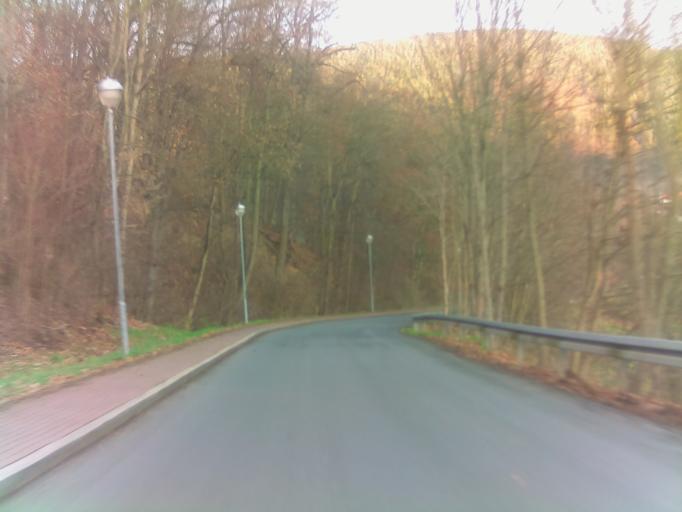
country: DE
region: Thuringia
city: Reinstadt
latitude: 50.7316
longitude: 11.4494
